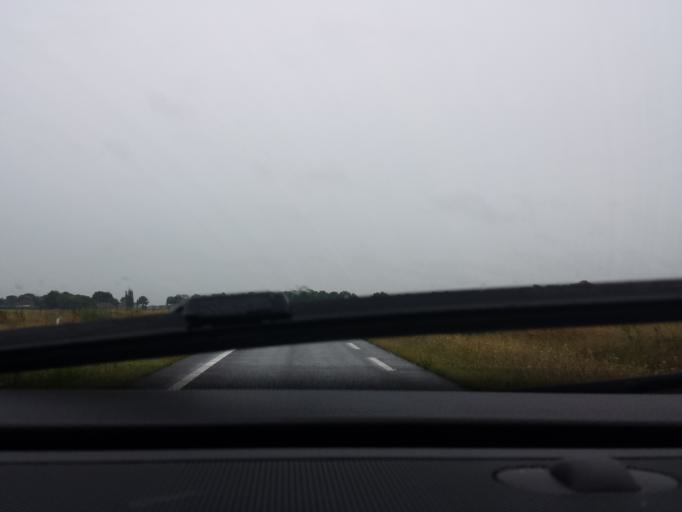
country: NL
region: Gelderland
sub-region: Gemeente Montferland
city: s-Heerenberg
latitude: 51.9039
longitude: 6.2739
